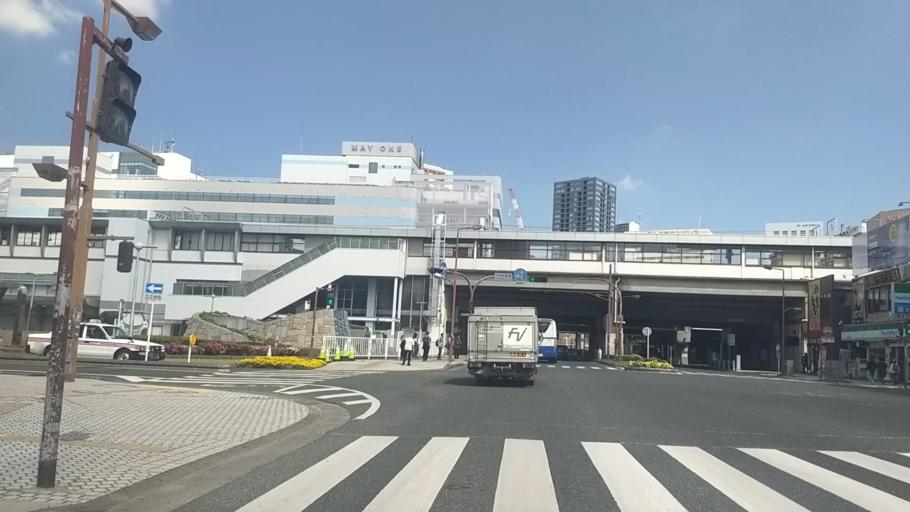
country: JP
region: Shizuoka
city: Hamamatsu
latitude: 34.7032
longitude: 137.7361
